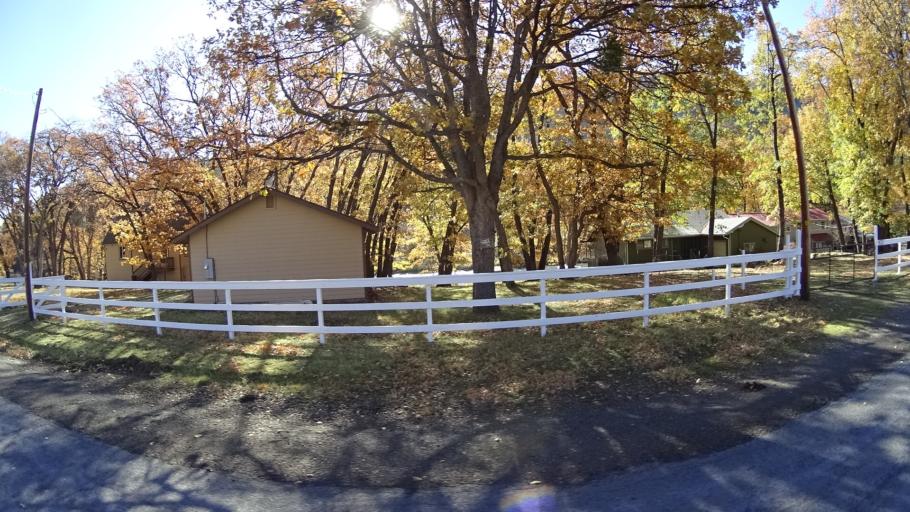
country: US
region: California
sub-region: Siskiyou County
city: Montague
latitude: 41.9657
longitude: -122.2596
